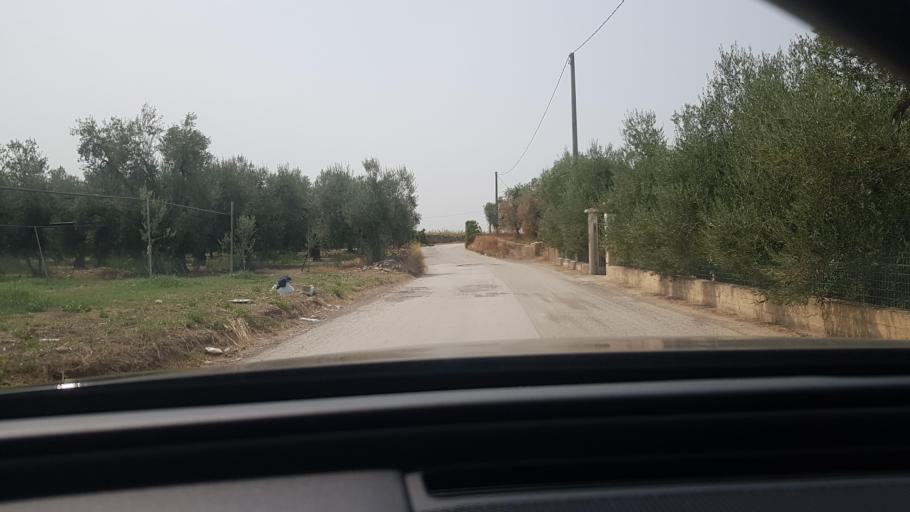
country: IT
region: Apulia
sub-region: Provincia di Barletta - Andria - Trani
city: Andria
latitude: 41.2227
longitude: 16.2656
